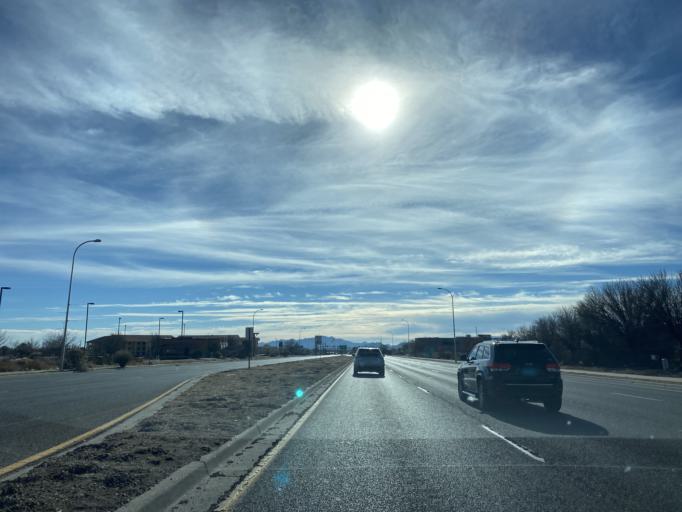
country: US
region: New Mexico
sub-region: Santa Fe County
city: Agua Fria
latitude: 35.6380
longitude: -106.0180
